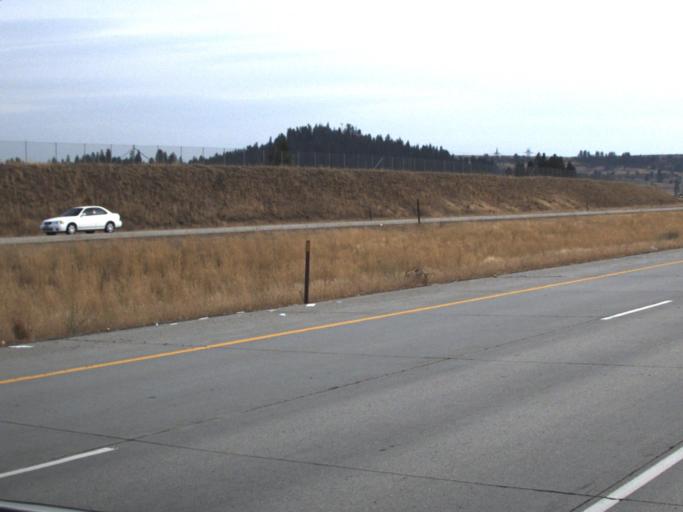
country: US
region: Washington
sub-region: Spokane County
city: Mead
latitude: 47.7629
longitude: -117.3671
